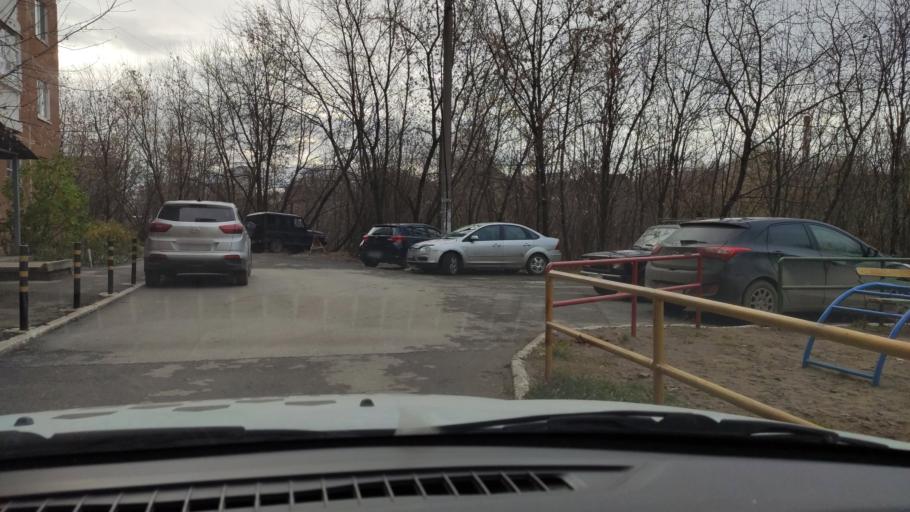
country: RU
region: Perm
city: Perm
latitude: 57.9762
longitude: 56.2722
